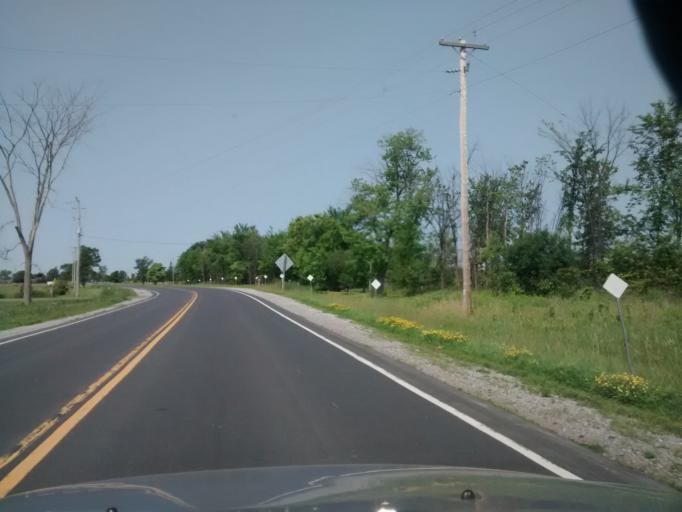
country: CA
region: Ontario
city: Hamilton
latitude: 42.9681
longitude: -79.7796
